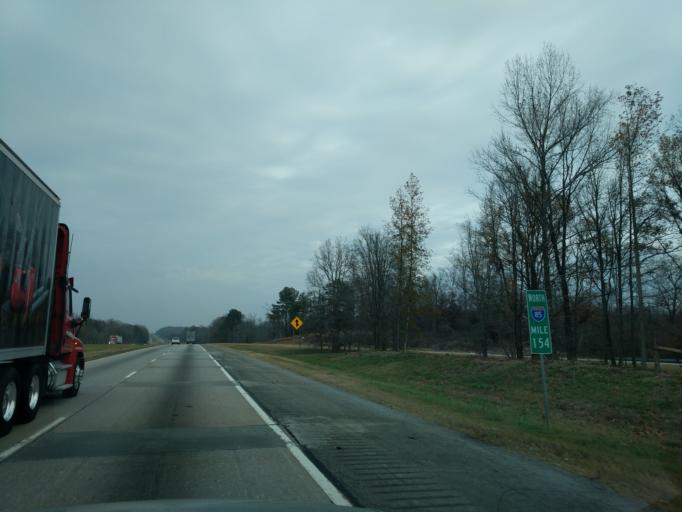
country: US
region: Georgia
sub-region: Banks County
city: Homer
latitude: 34.2976
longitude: -83.4072
